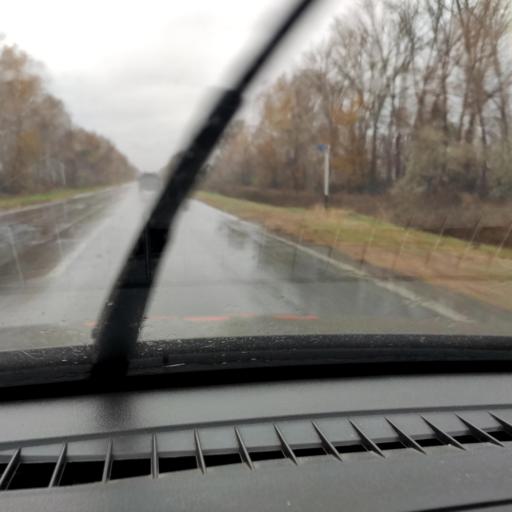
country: RU
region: Samara
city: Tol'yatti
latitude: 53.6668
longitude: 49.2779
